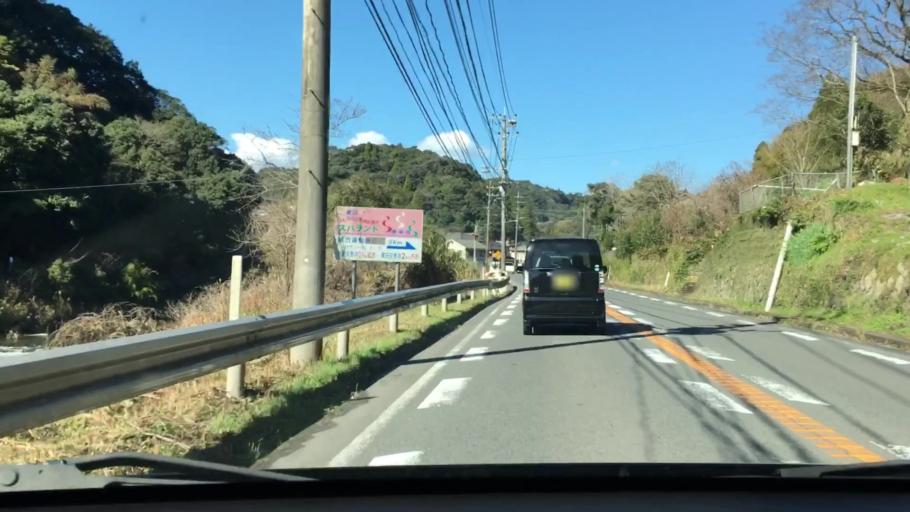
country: JP
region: Kagoshima
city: Kagoshima-shi
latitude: 31.6489
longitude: 130.5135
